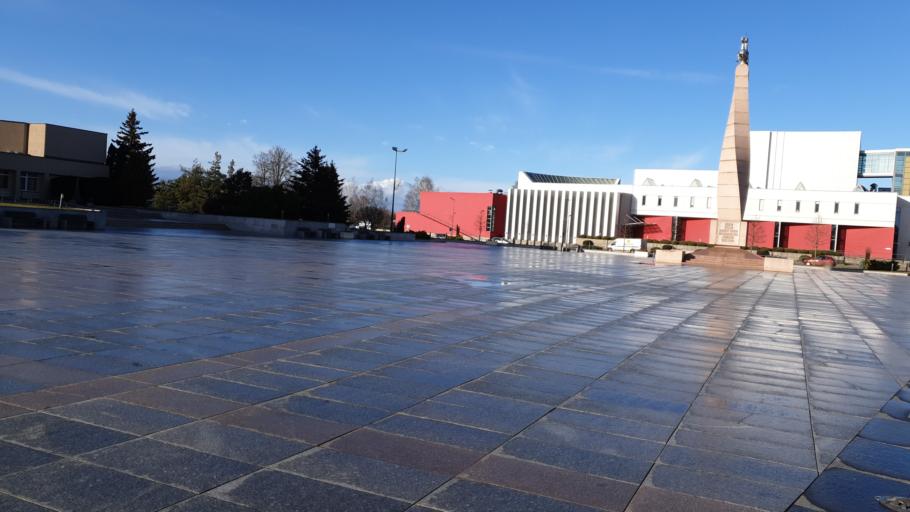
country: LT
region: Marijampoles apskritis
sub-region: Marijampole Municipality
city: Marijampole
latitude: 54.5570
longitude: 23.3495
